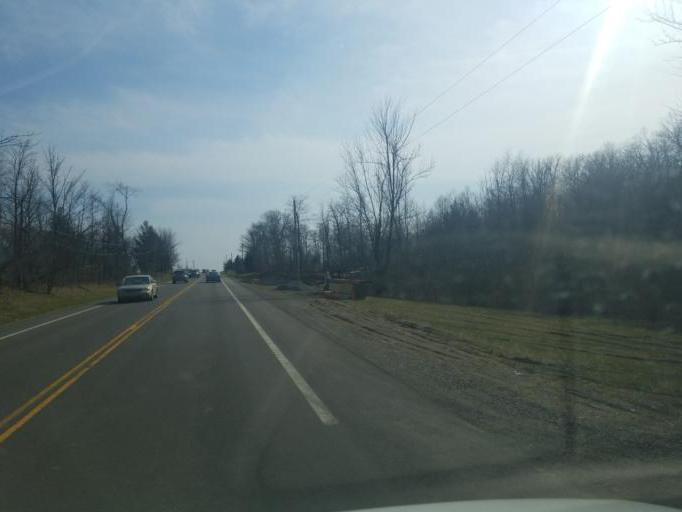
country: US
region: Ohio
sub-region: Logan County
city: Northwood
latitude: 40.4359
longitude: -83.7364
